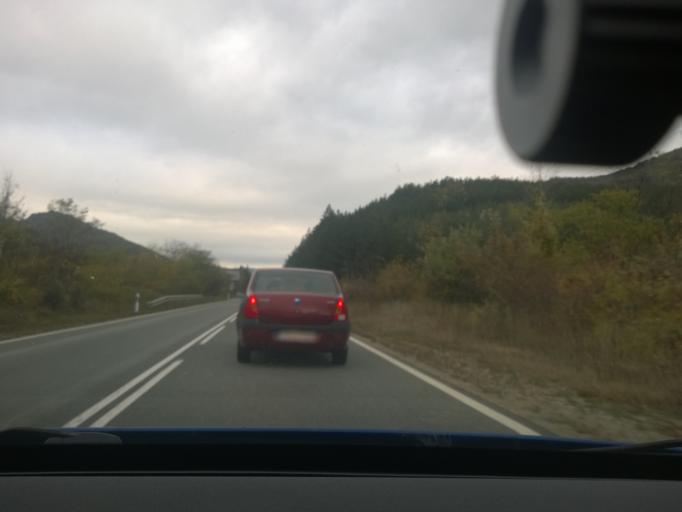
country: BG
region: Sofiya
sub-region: Obshtina Dragoman
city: Dragoman
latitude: 42.9589
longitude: 22.9017
